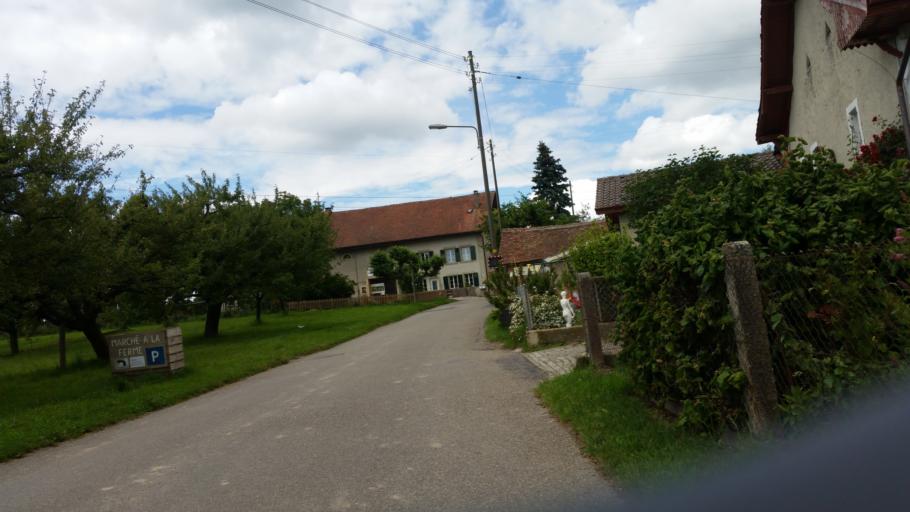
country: CH
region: Vaud
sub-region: Lausanne District
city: Le Mont-sur-Lausanne
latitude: 46.5663
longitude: 6.6268
